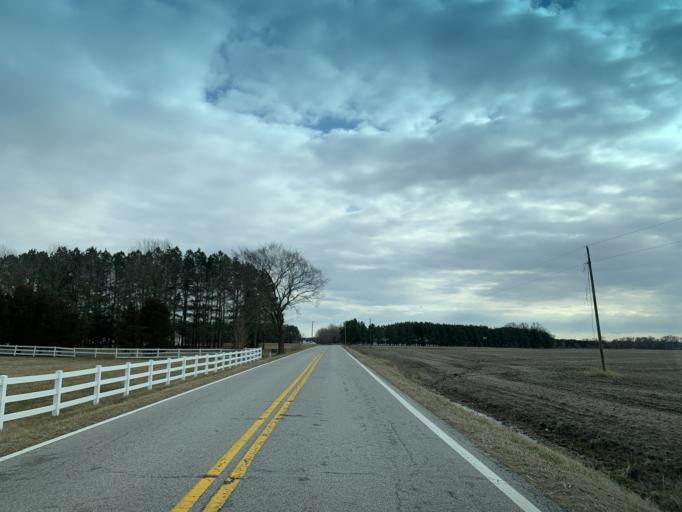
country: US
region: Maryland
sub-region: Caroline County
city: Ridgely
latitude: 38.9609
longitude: -75.9791
